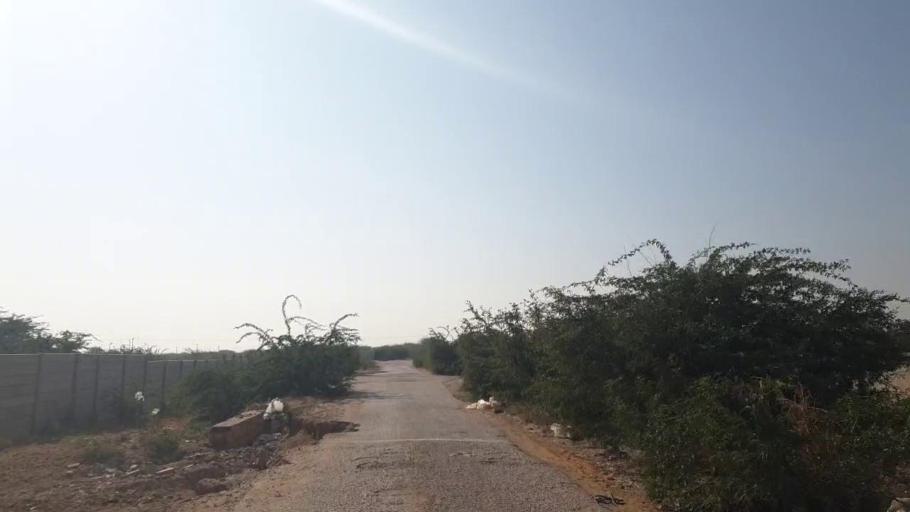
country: PK
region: Sindh
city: Thatta
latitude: 25.1539
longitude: 67.7739
